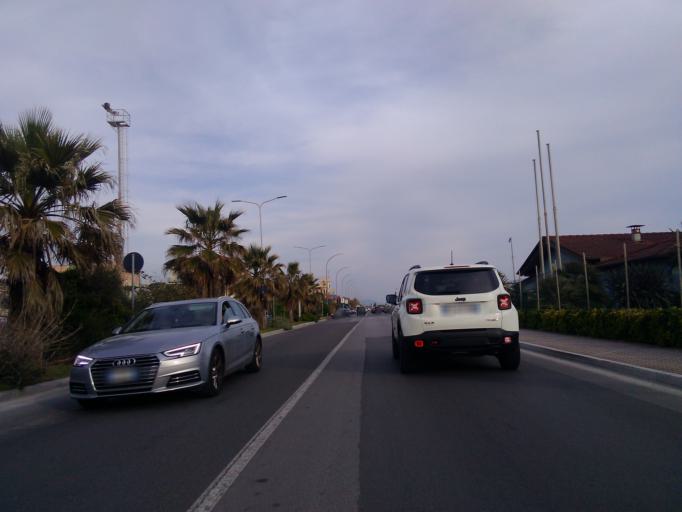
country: IT
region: Tuscany
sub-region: Provincia di Massa-Carrara
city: Massa
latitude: 44.0111
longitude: 10.0939
